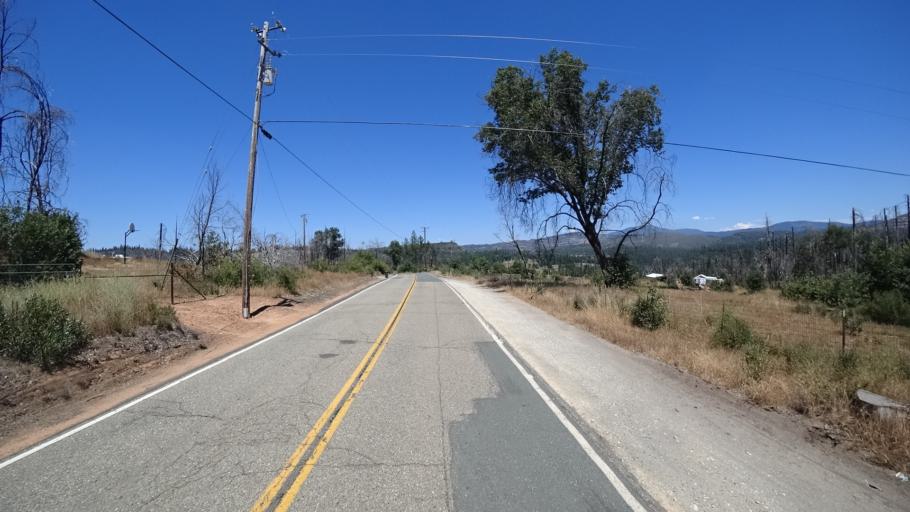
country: US
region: California
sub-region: Calaveras County
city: Mountain Ranch
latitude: 38.2621
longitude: -120.5120
